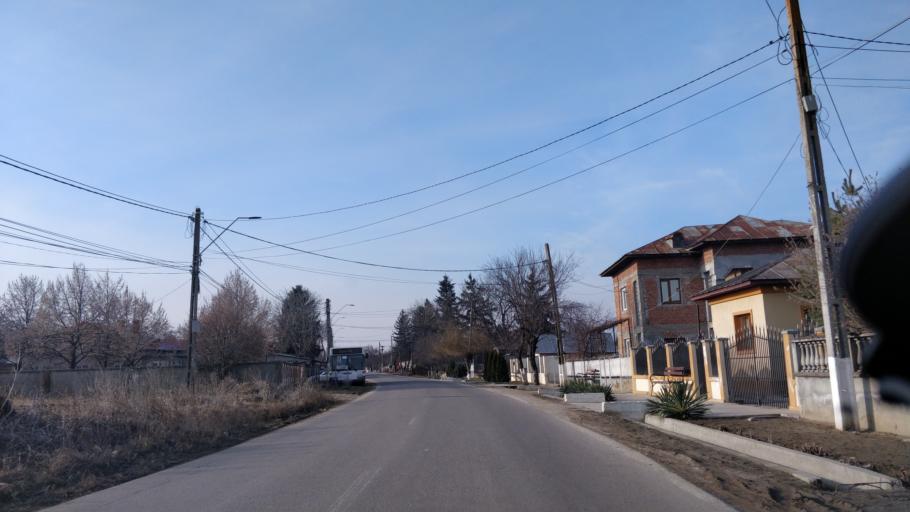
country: RO
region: Giurgiu
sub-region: Comuna Ulmi
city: Ulmi
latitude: 44.4971
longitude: 25.7710
